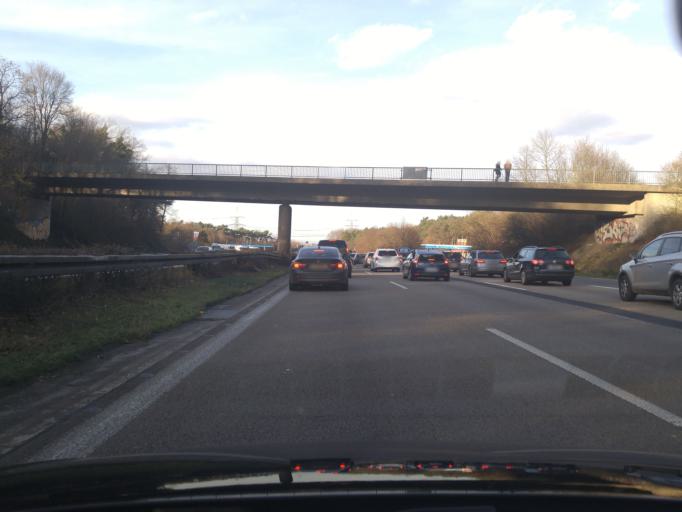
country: DE
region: North Rhine-Westphalia
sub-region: Regierungsbezirk Dusseldorf
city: Hilden
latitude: 51.1550
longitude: 6.9650
